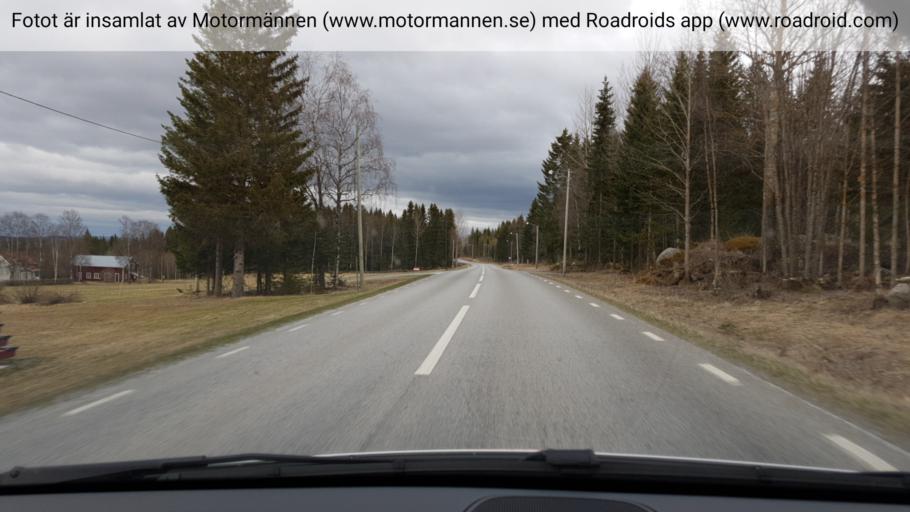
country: SE
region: Jaemtland
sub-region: Krokoms Kommun
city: Krokom
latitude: 63.1531
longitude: 14.1521
